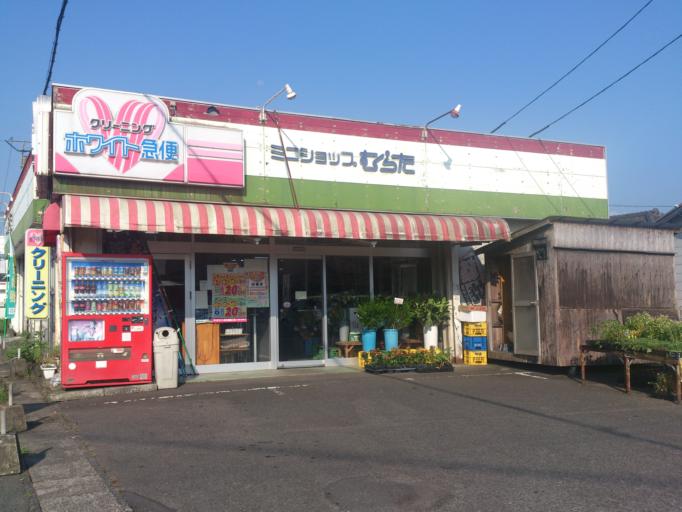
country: JP
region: Kagoshima
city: Kanoya
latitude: 31.3455
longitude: 130.9360
